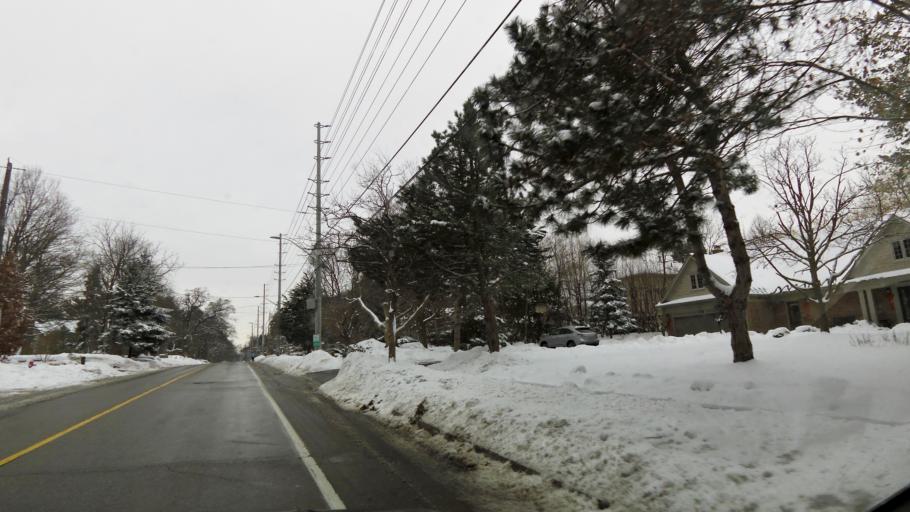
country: CA
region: Ontario
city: Mississauga
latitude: 43.5413
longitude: -79.6151
